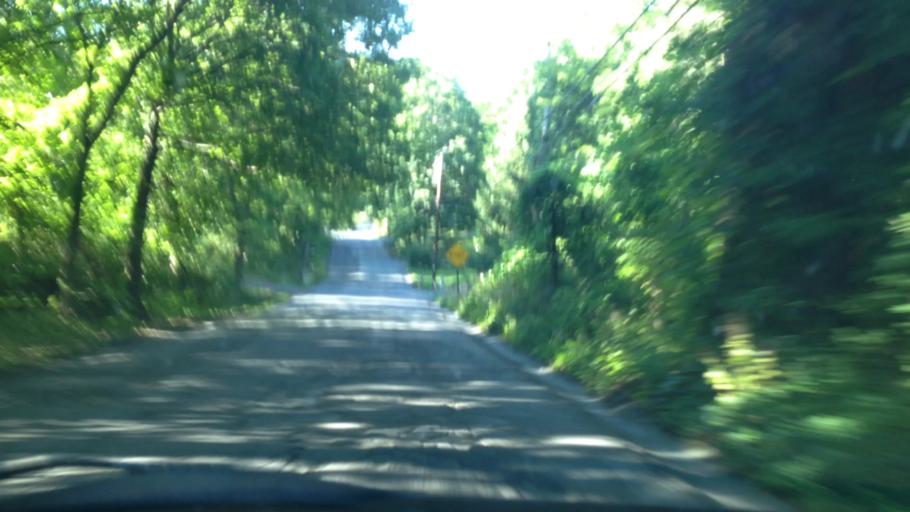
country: US
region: New York
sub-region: Ulster County
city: Tillson
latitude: 41.8194
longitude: -74.0457
